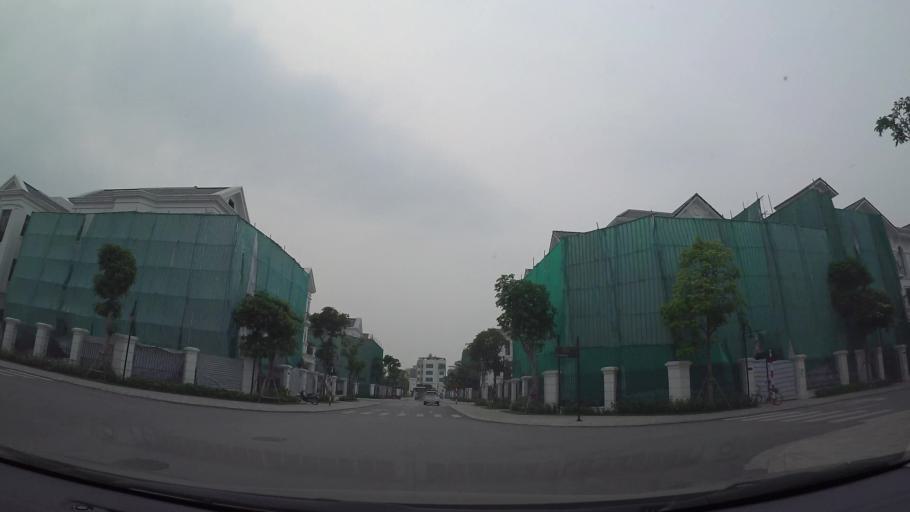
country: VN
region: Ha Noi
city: Trau Quy
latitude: 21.0493
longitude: 105.9040
